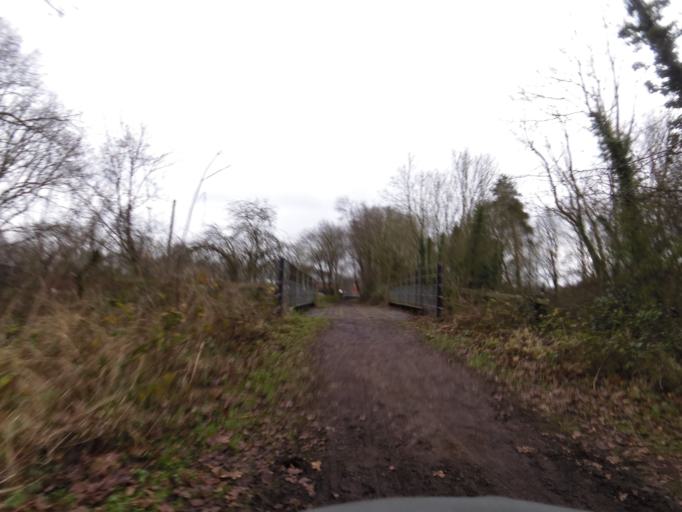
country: GB
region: England
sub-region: Norfolk
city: Briston
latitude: 52.7526
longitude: 1.0976
